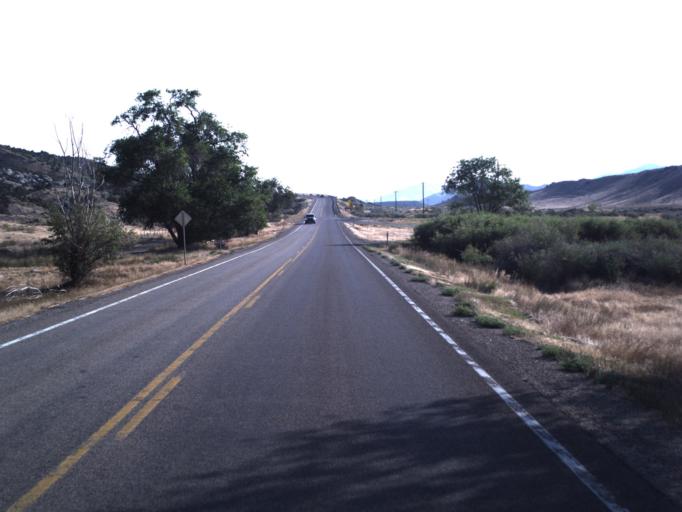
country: US
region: Utah
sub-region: Uintah County
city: Vernal
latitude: 40.5066
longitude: -109.5273
